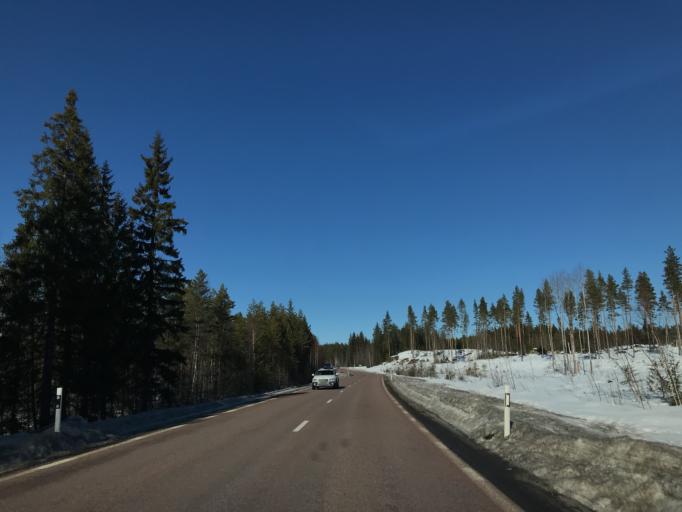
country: SE
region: Dalarna
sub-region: Vansbro Kommun
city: Vansbro
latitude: 60.4788
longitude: 14.2356
